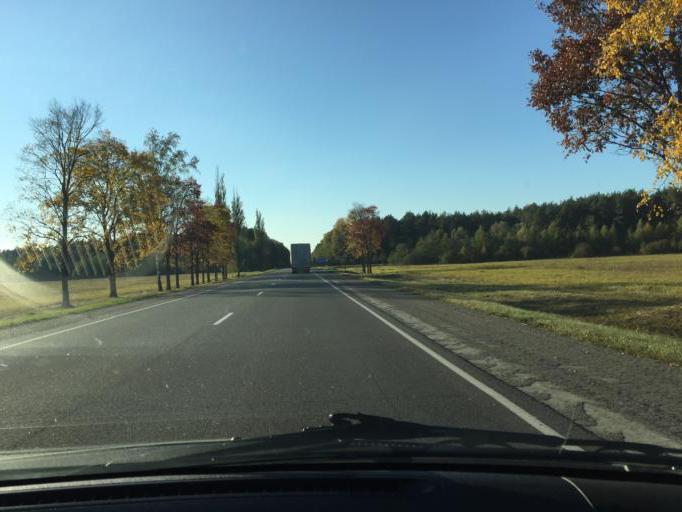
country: BY
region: Brest
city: Luninyets
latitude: 52.2761
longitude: 26.8699
